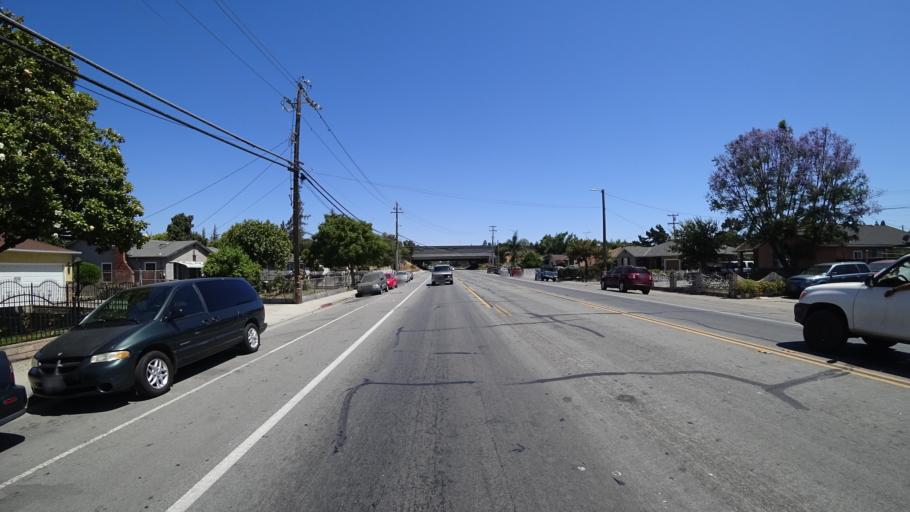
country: US
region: California
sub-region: Santa Clara County
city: San Jose
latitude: 37.3378
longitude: -121.8586
